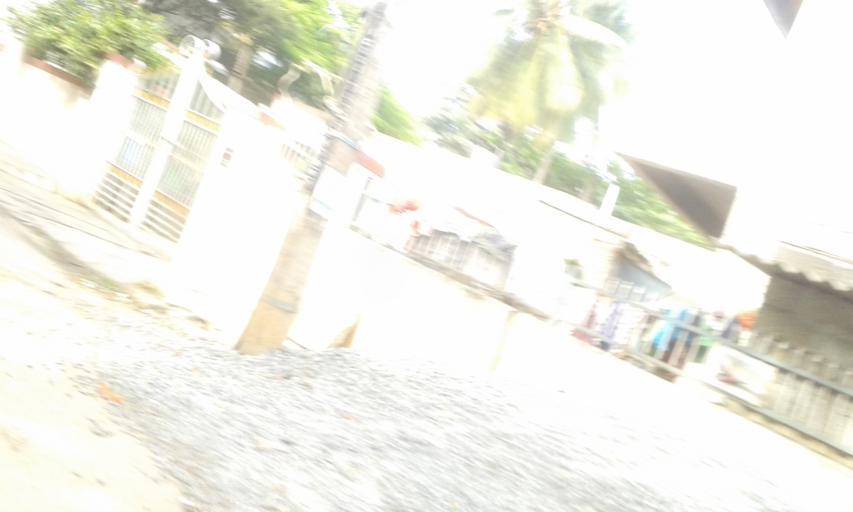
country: IN
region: Karnataka
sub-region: Bangalore Urban
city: Bangalore
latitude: 12.9358
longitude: 77.6279
